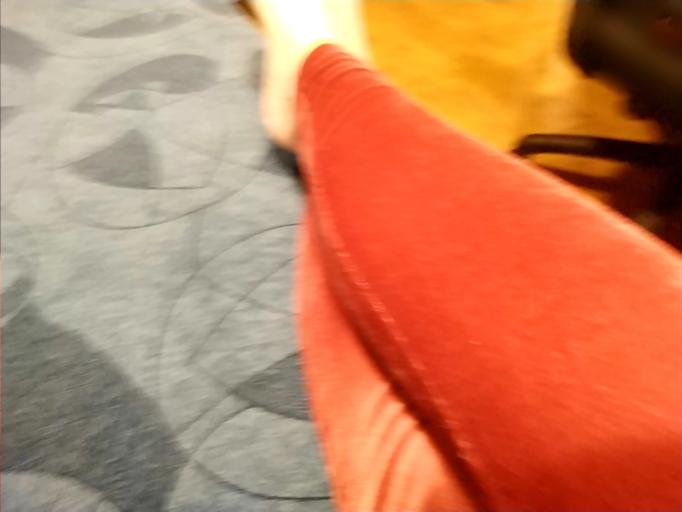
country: RU
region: Novgorod
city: Kulotino
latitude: 58.4039
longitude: 33.4518
